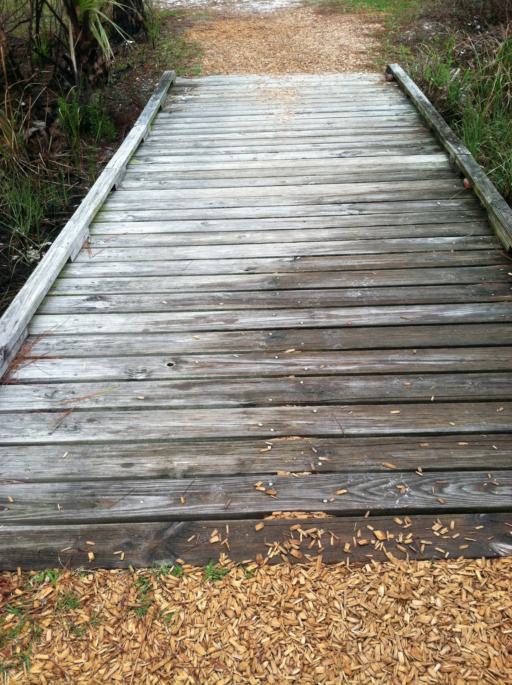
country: US
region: Florida
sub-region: Gulf County
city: Port Saint Joe
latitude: 29.7784
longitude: -85.4070
